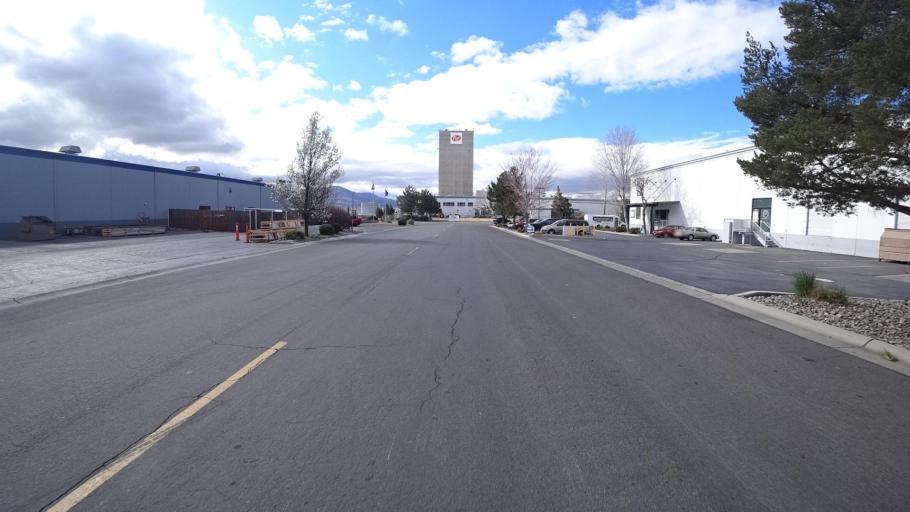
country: US
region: Nevada
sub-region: Washoe County
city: Sparks
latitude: 39.5223
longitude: -119.7263
